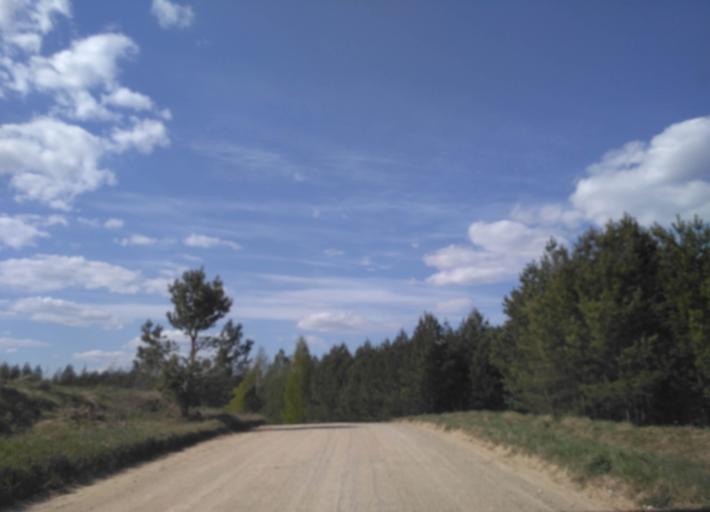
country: BY
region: Minsk
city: Narach
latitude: 54.9844
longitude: 26.6092
